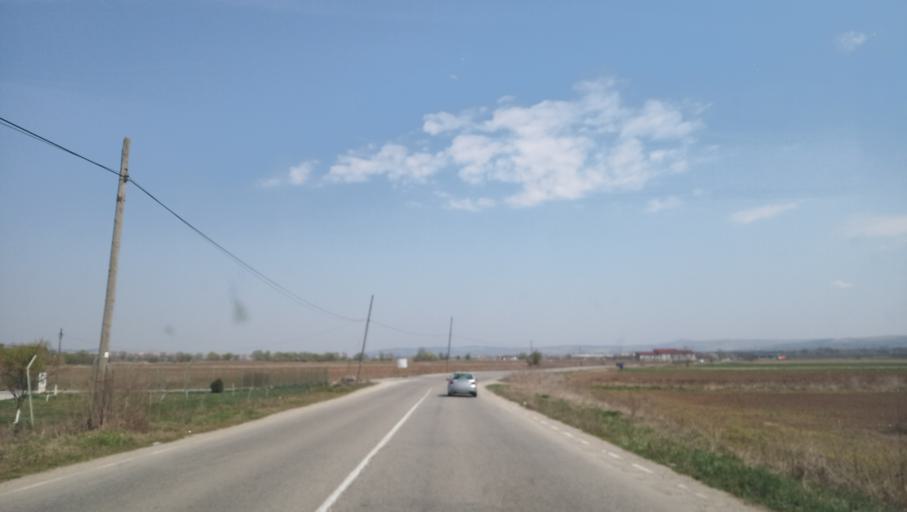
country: RO
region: Alba
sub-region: Municipiul Sebes
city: Lancram
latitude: 46.0218
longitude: 23.5265
